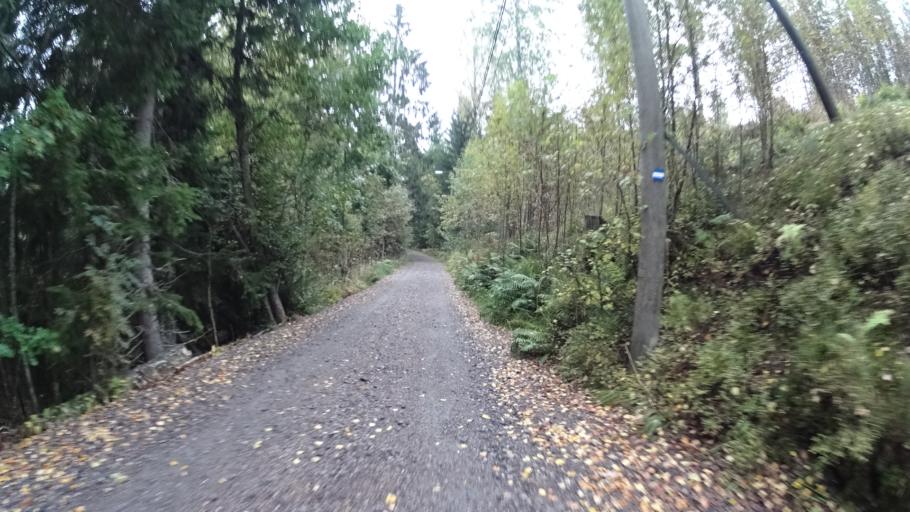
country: FI
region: Uusimaa
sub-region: Helsinki
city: Kauniainen
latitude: 60.3225
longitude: 24.7034
